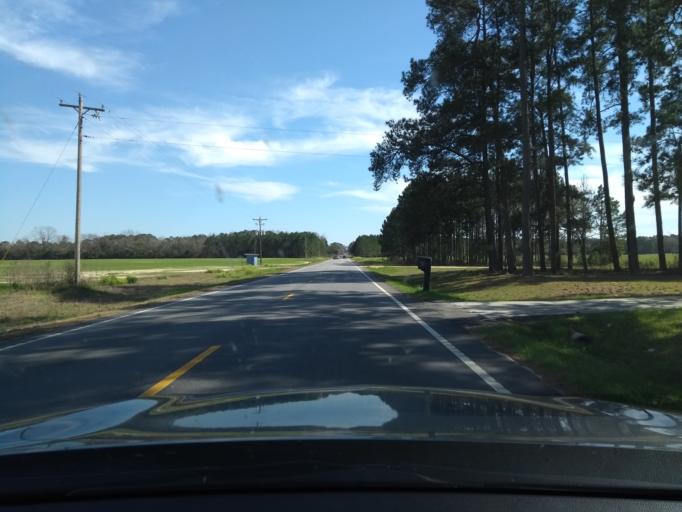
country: US
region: Georgia
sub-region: Bulloch County
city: Brooklet
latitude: 32.4769
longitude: -81.6112
